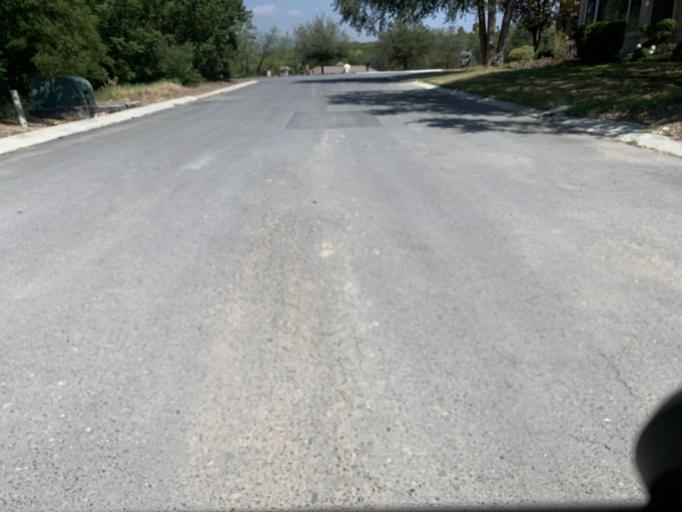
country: MX
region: Nuevo Leon
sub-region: Juarez
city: Bosques de San Pedro
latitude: 25.5205
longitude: -100.1933
